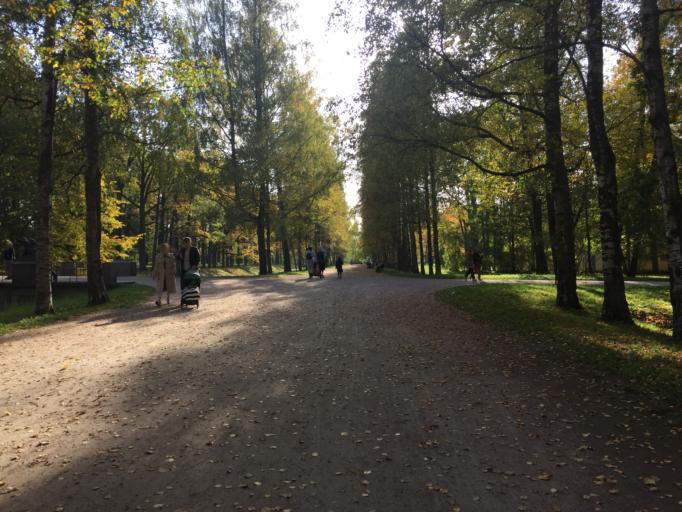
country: RU
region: St.-Petersburg
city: Pushkin
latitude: 59.7195
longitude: 30.3857
